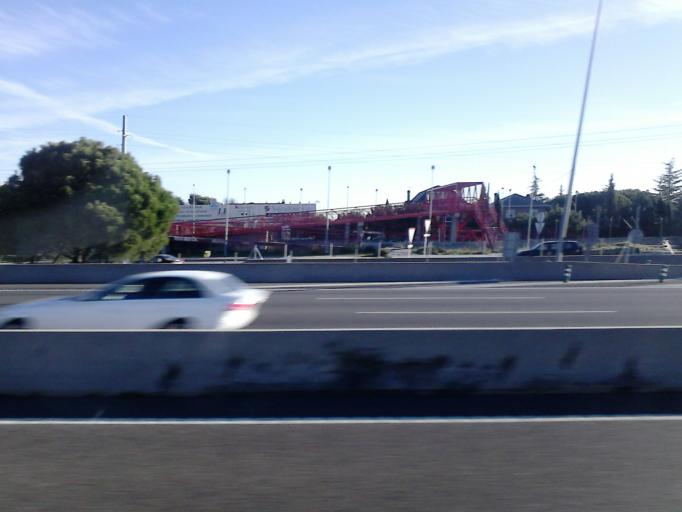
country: ES
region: Madrid
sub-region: Provincia de Madrid
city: Las Matas
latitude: 40.5568
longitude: -3.9003
